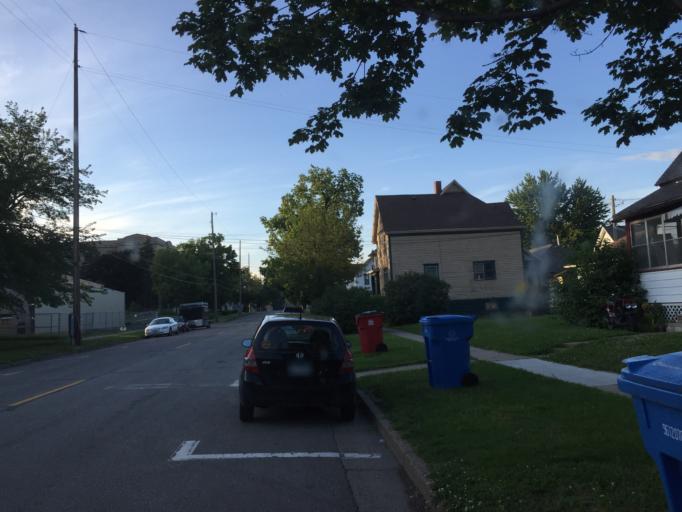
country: US
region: Minnesota
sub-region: Winona County
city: Winona
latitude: 44.0514
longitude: -91.6659
